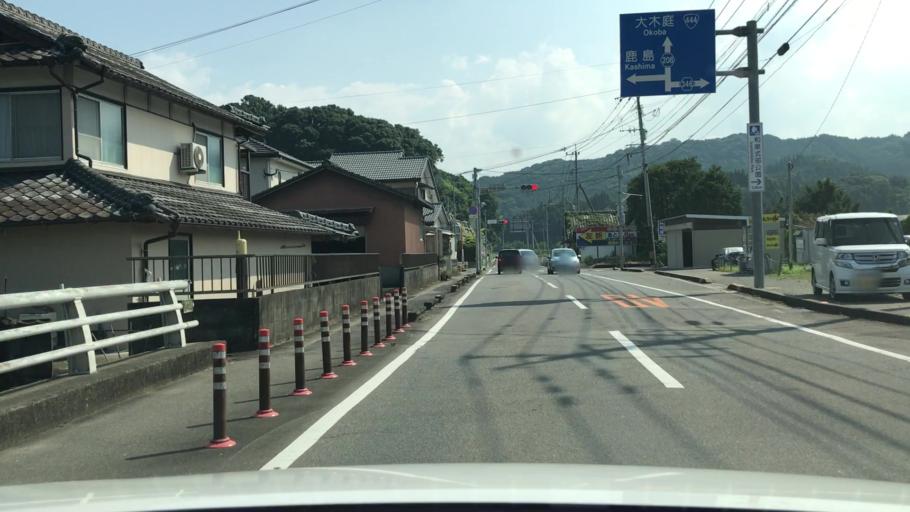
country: JP
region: Saga Prefecture
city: Kashima
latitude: 33.1222
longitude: 130.0638
